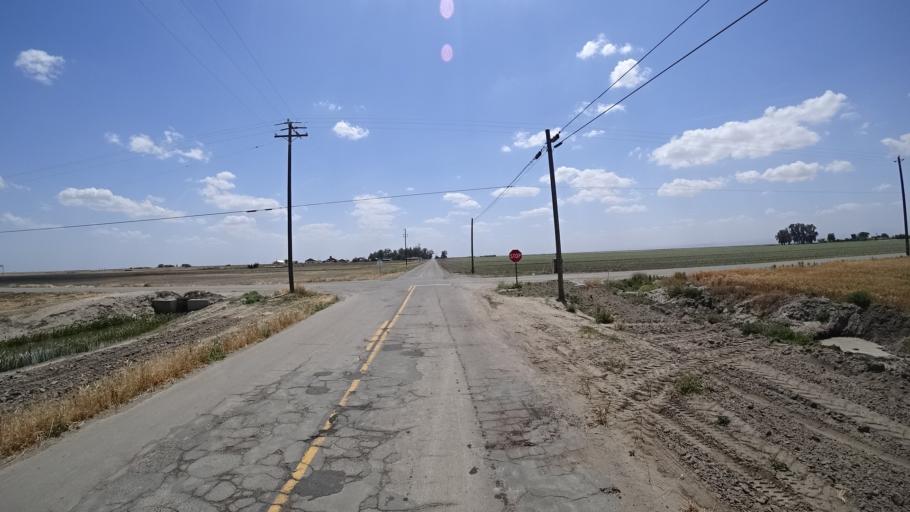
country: US
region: California
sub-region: Kings County
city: Stratford
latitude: 36.1677
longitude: -119.8161
